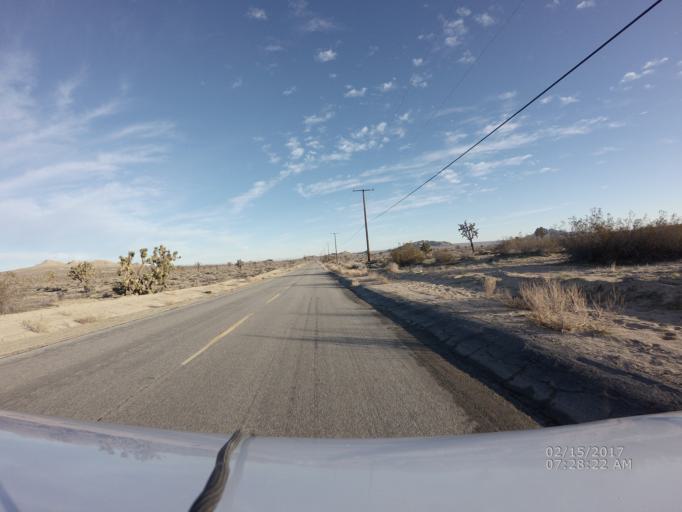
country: US
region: California
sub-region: Los Angeles County
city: Lake Los Angeles
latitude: 34.6116
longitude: -117.8715
